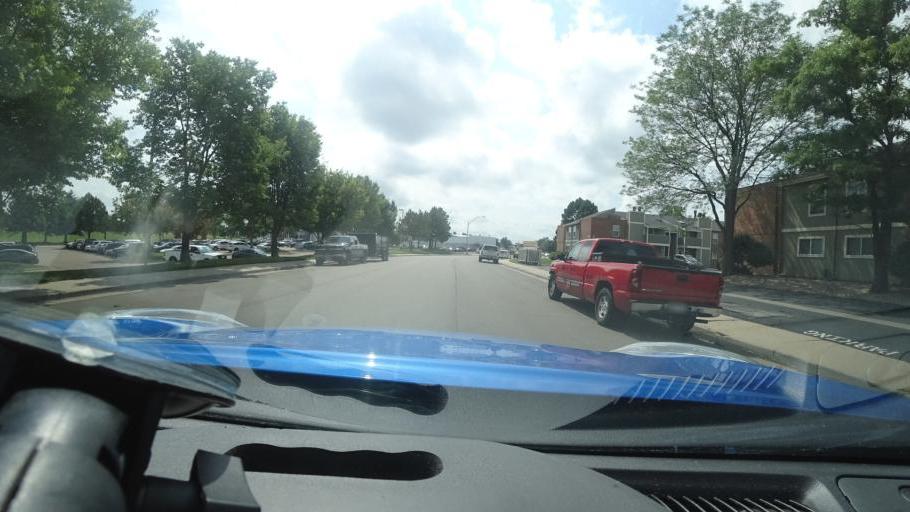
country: US
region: Colorado
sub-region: Adams County
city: Aurora
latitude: 39.7080
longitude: -104.8690
